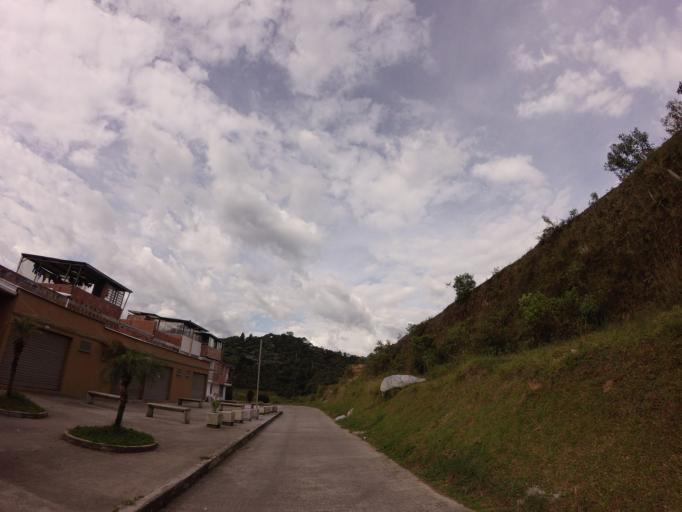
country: CO
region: Caldas
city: Manizales
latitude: 5.0759
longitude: -75.5040
